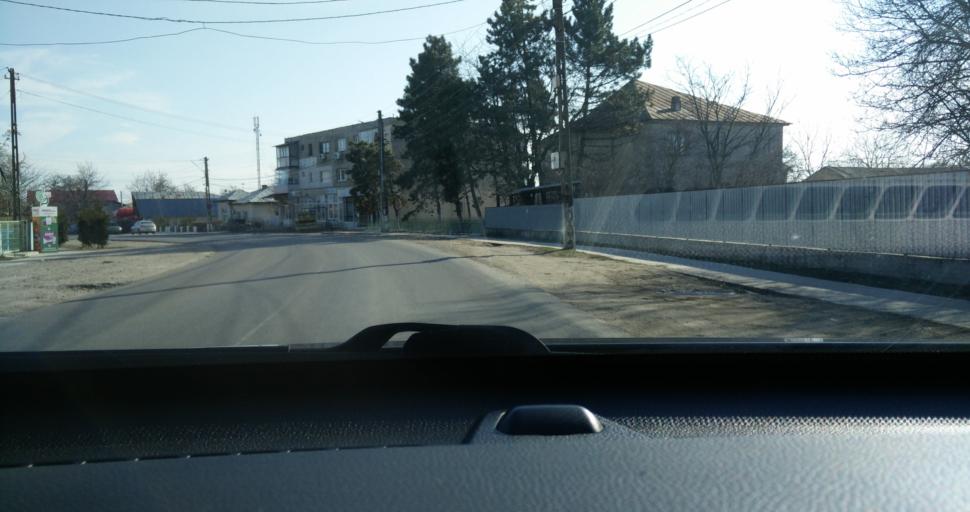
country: RO
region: Vrancea
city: Vulturu de Sus
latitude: 45.6193
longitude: 27.4228
